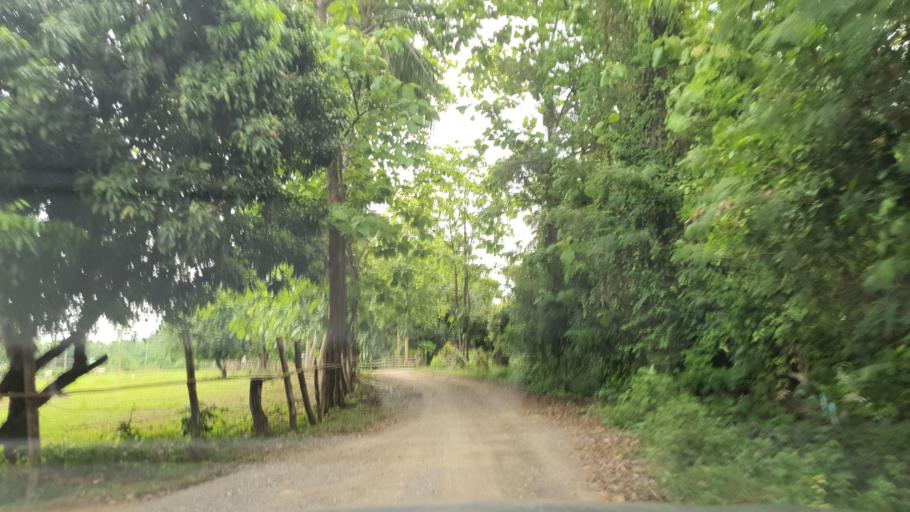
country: TH
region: Sukhothai
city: Thung Saliam
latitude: 17.2484
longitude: 99.5468
